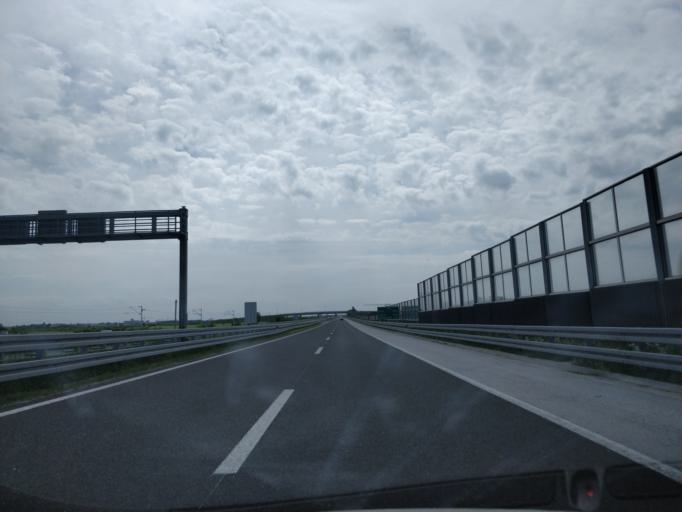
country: HR
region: Grad Zagreb
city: Odra
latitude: 45.7317
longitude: 16.0140
